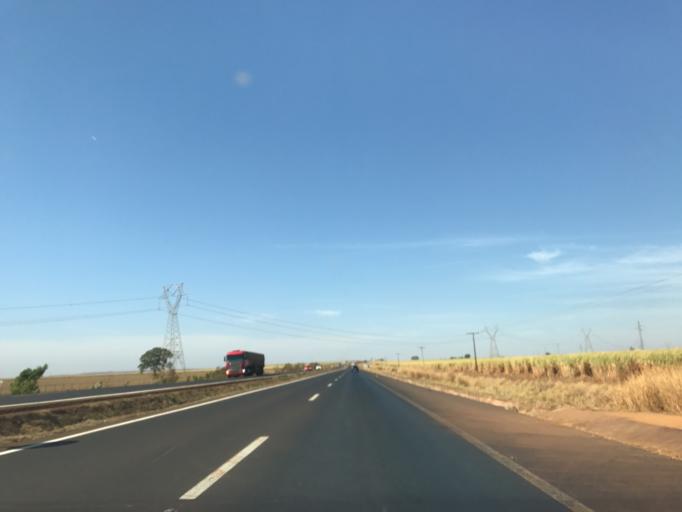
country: BR
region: Minas Gerais
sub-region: Centralina
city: Centralina
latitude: -18.5035
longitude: -49.1889
